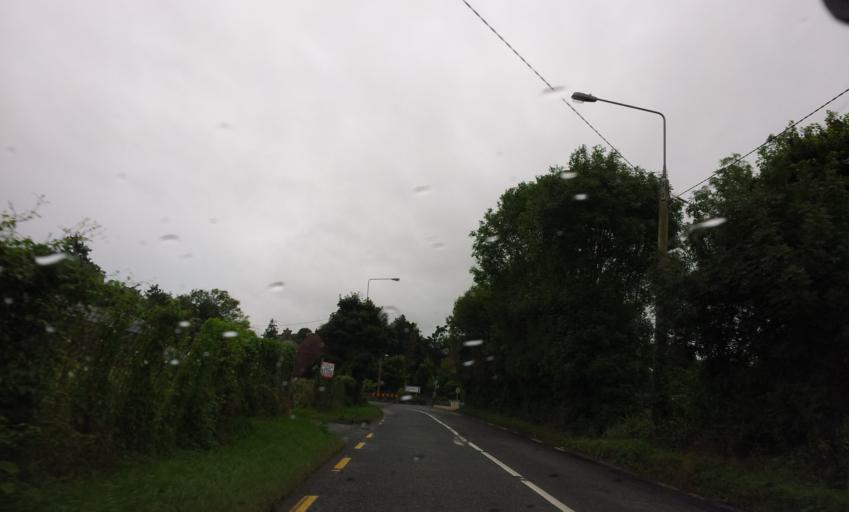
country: IE
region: Munster
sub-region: County Cork
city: Mitchelstown
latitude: 52.2440
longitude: -8.4505
